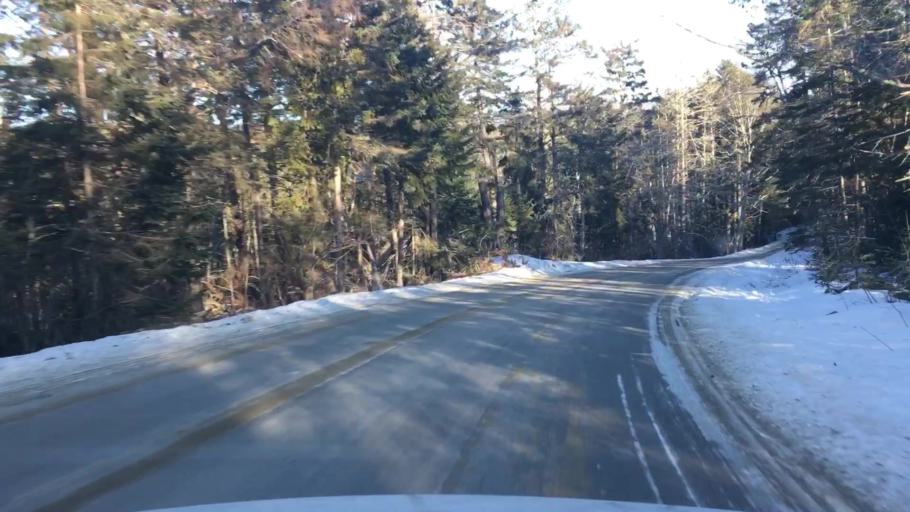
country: US
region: Maine
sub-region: Hancock County
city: Castine
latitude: 44.3601
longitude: -68.7590
